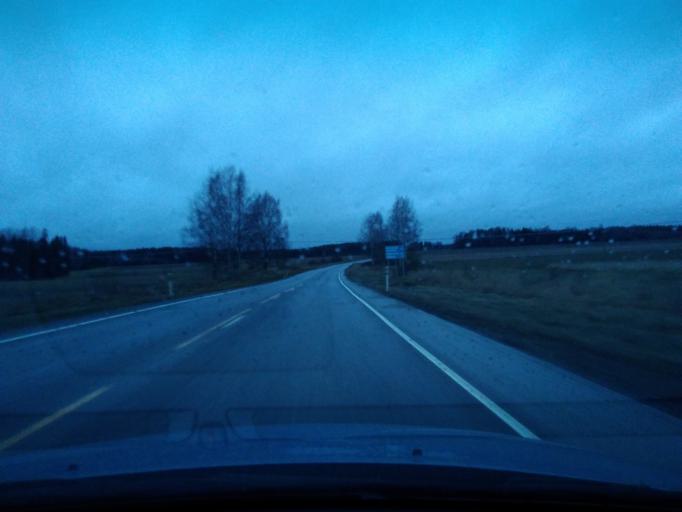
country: FI
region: Uusimaa
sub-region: Porvoo
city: Porvoo
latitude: 60.3948
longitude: 25.6032
